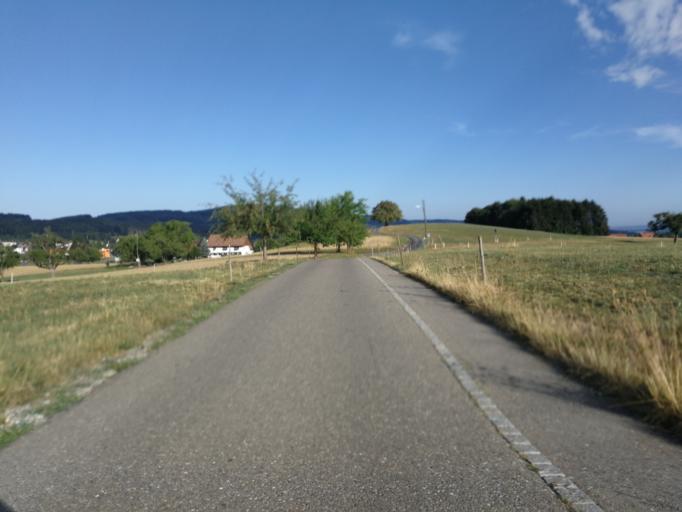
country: CH
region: Zurich
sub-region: Bezirk Meilen
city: Oetwil am See
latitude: 47.2720
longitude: 8.7386
